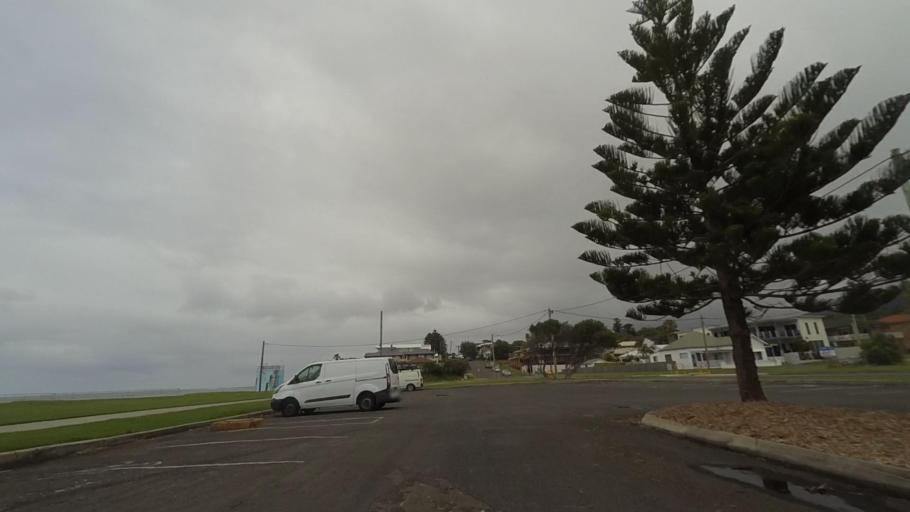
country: AU
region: New South Wales
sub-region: Wollongong
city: Bulli
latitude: -34.3179
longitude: 150.9263
